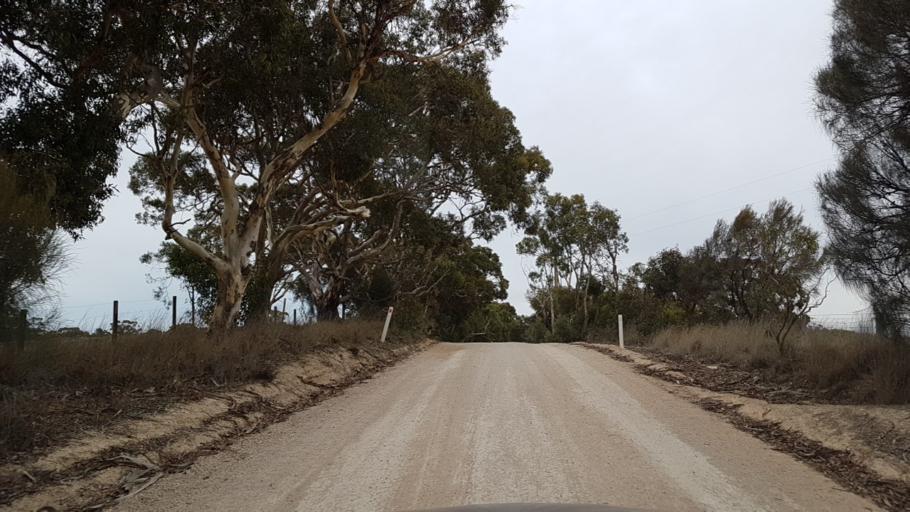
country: AU
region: South Australia
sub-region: Mount Barker
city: Nairne
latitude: -34.9982
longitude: 138.9743
